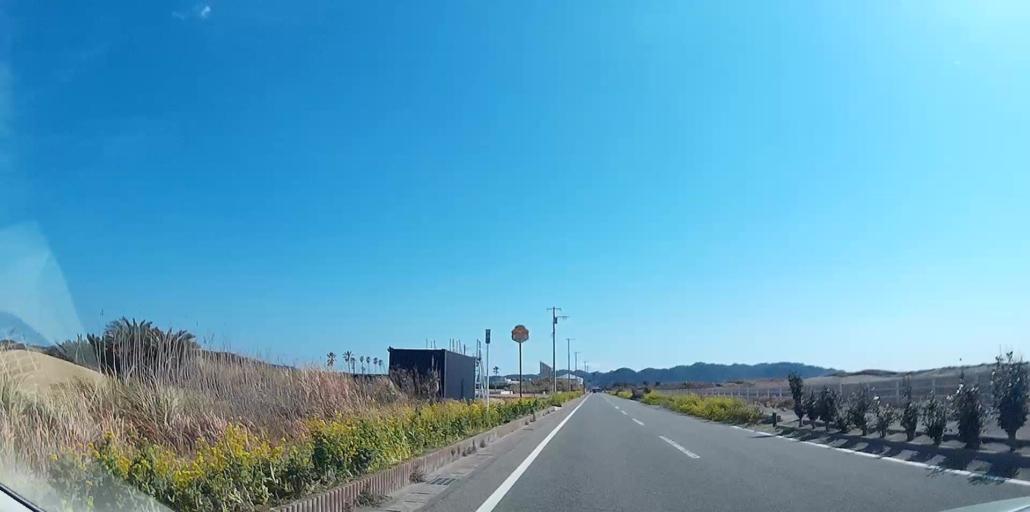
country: JP
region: Chiba
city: Tateyama
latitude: 34.9431
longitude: 139.8175
